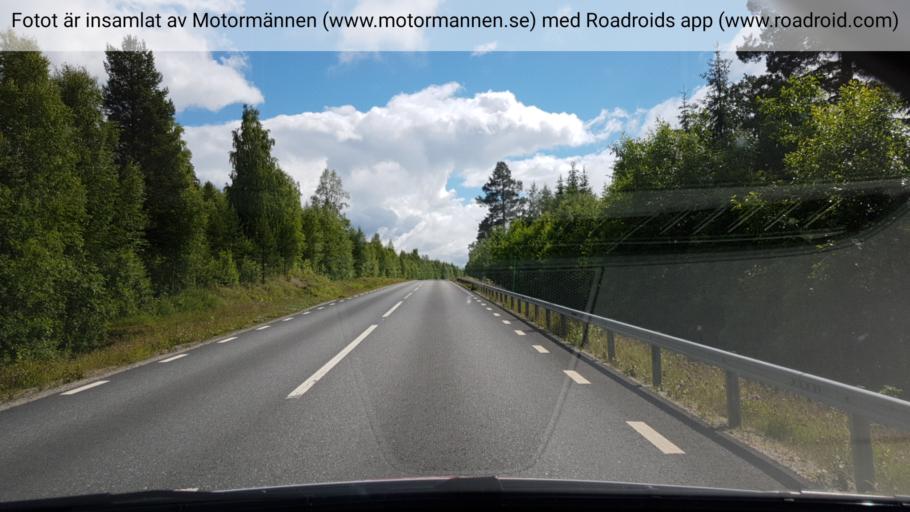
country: SE
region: Vaesterbotten
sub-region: Bjurholms Kommun
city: Bjurholm
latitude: 64.3255
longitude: 19.1555
